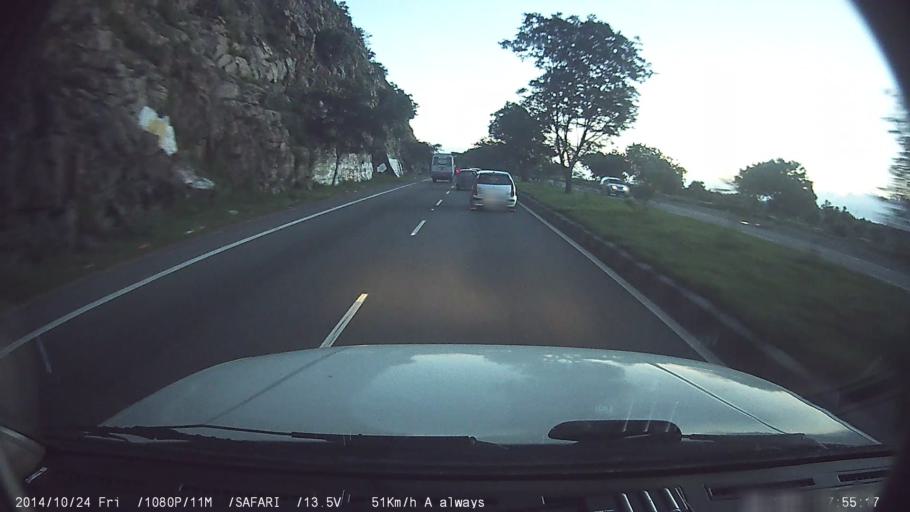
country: IN
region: Tamil Nadu
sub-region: Kancheepuram
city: Chengalpattu
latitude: 12.6849
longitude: 79.9591
